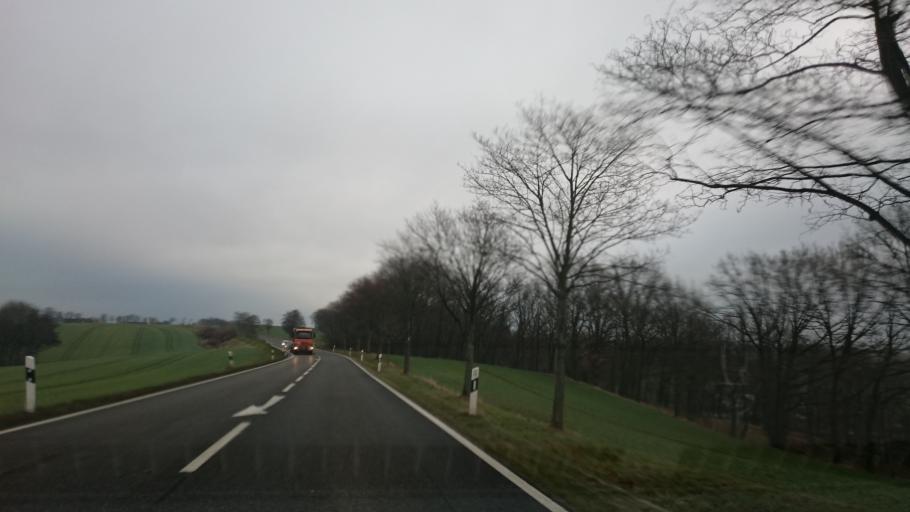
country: DE
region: Saxony
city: Mulsen
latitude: 50.7420
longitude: 12.5883
